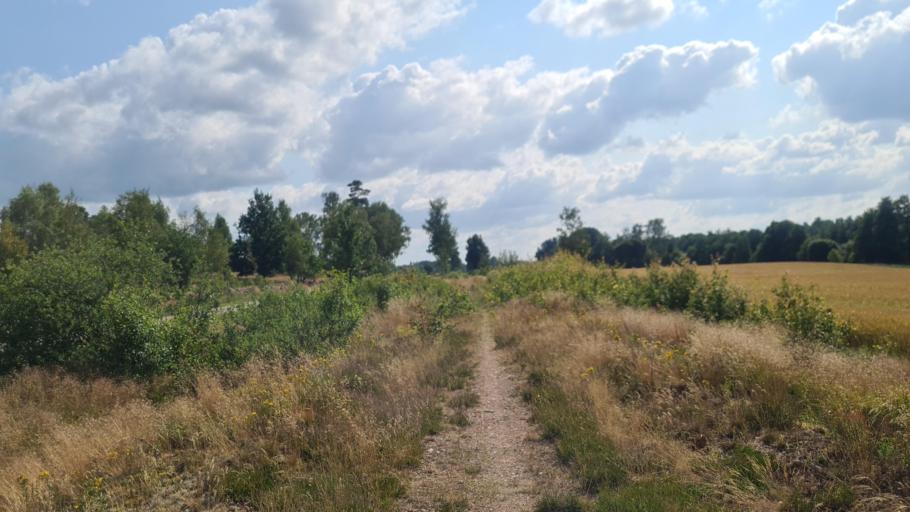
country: SE
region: Kronoberg
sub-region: Ljungby Kommun
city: Ljungby
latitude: 56.7497
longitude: 13.8821
